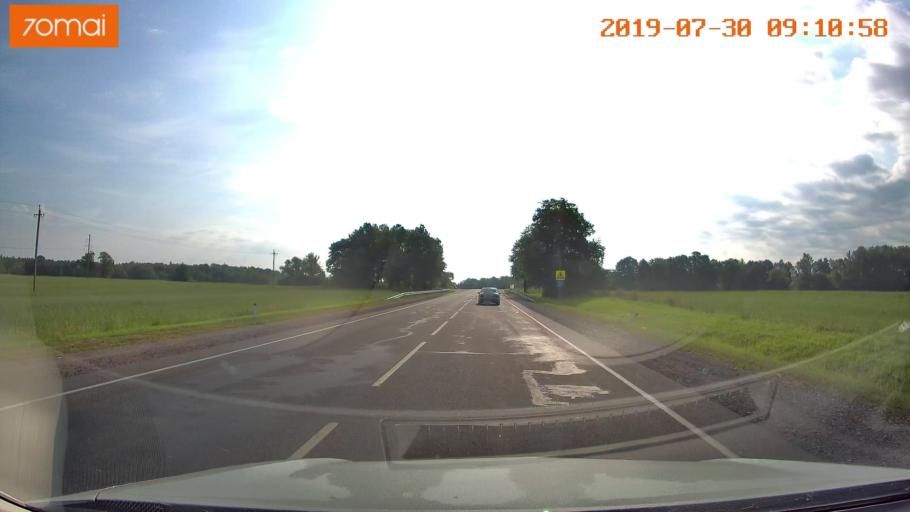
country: RU
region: Kaliningrad
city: Nesterov
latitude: 54.6118
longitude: 22.4404
